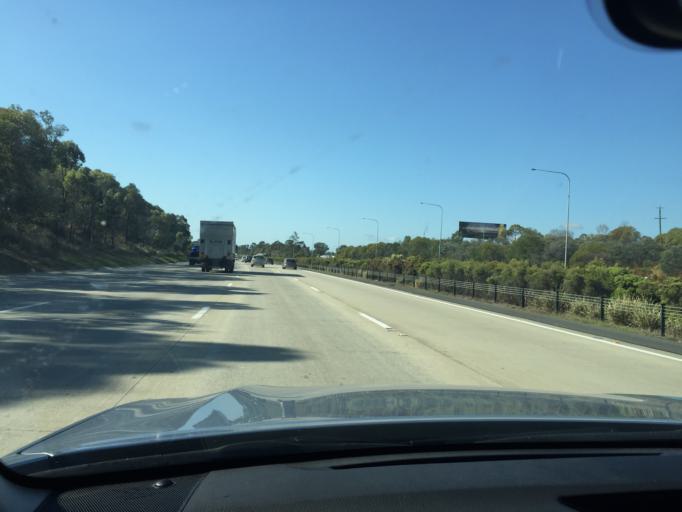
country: AU
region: Queensland
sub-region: Gold Coast
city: Yatala
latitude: -27.7528
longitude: 153.2371
